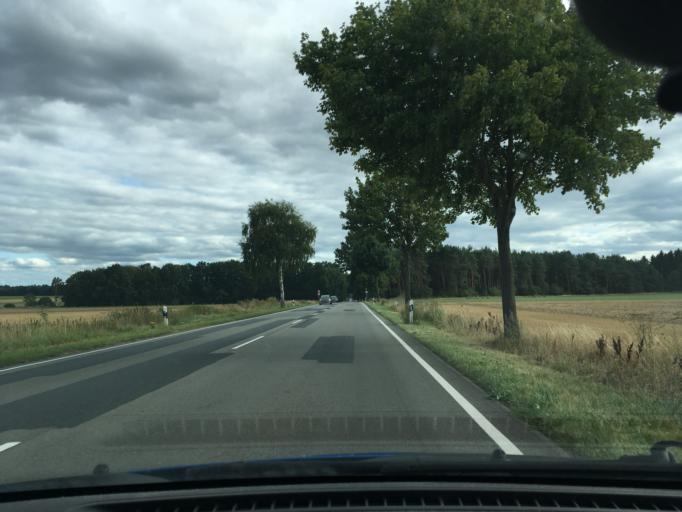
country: DE
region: Lower Saxony
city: Appel
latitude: 53.4115
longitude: 9.7892
